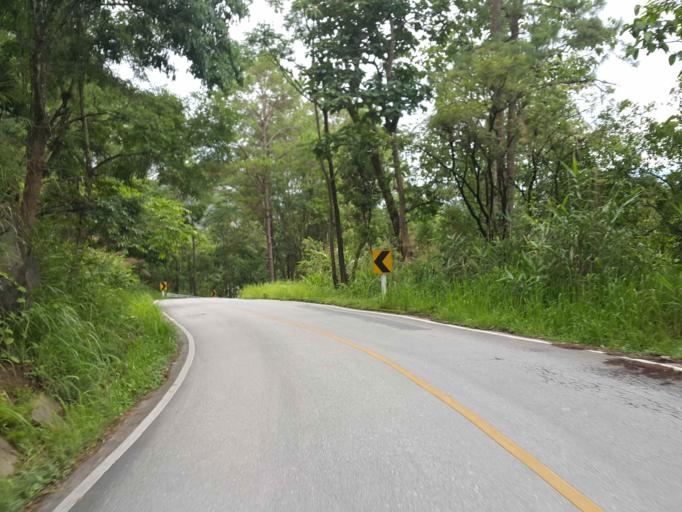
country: TH
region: Chiang Mai
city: Mae Chaem
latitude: 18.5147
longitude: 98.4466
